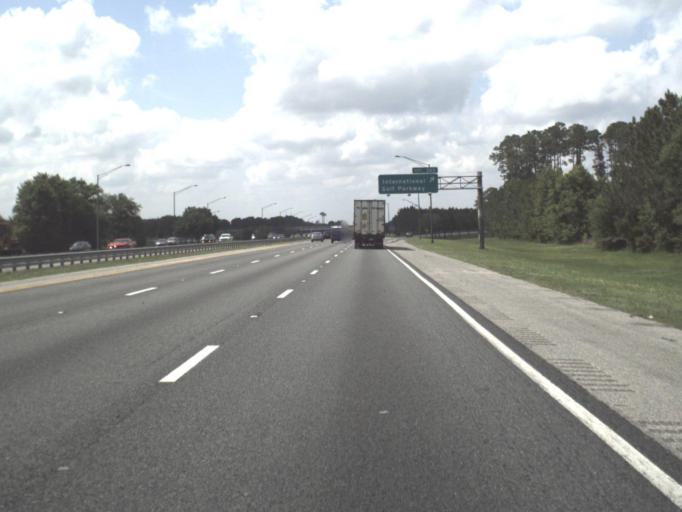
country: US
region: Florida
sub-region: Saint Johns County
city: Villano Beach
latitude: 29.9806
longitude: -81.4583
